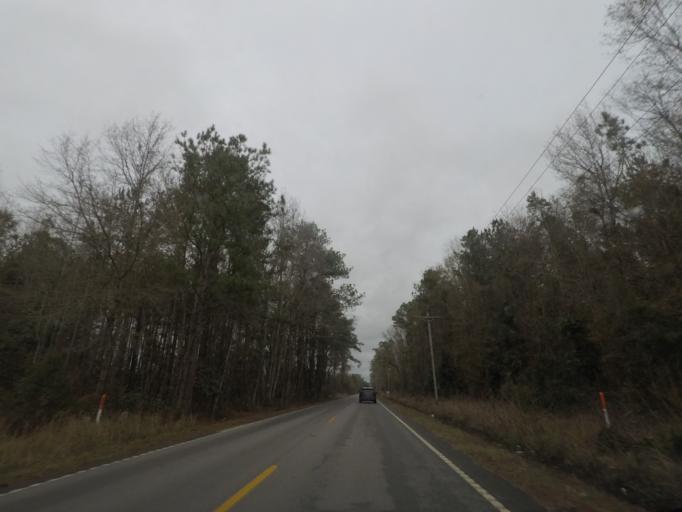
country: US
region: South Carolina
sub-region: Colleton County
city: Walterboro
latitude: 32.8582
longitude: -80.4900
